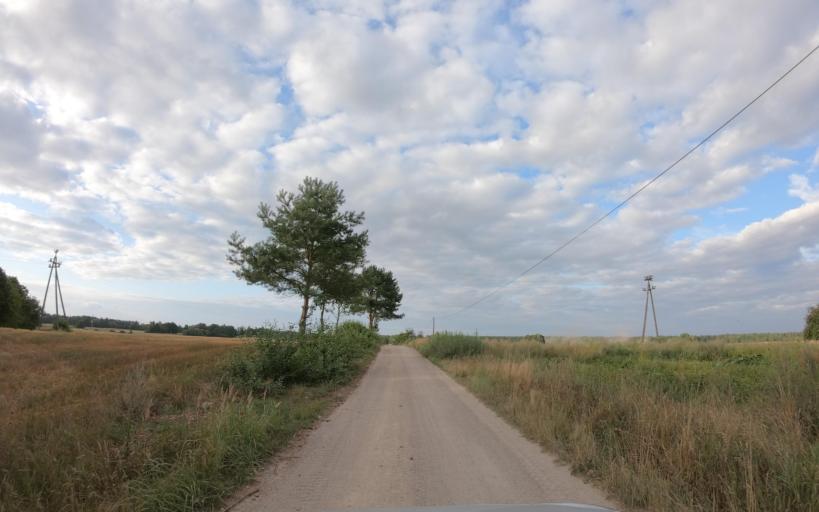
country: PL
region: West Pomeranian Voivodeship
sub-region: Powiat drawski
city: Wierzchowo
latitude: 53.5264
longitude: 16.1532
